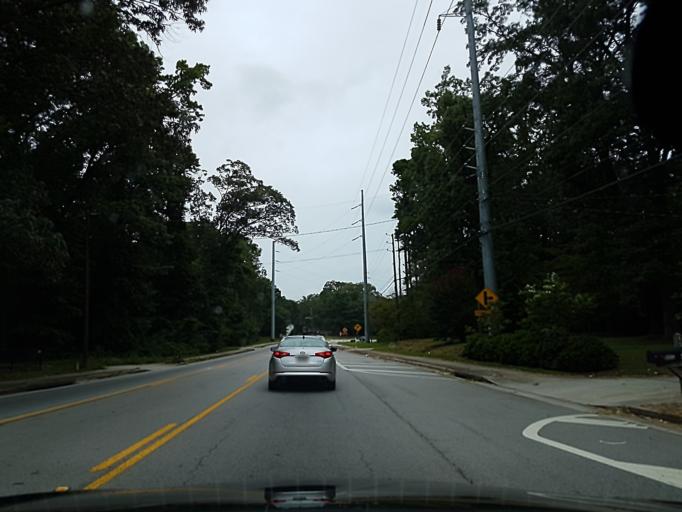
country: US
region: Georgia
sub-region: DeKalb County
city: Clarkston
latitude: 33.8286
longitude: -84.2586
